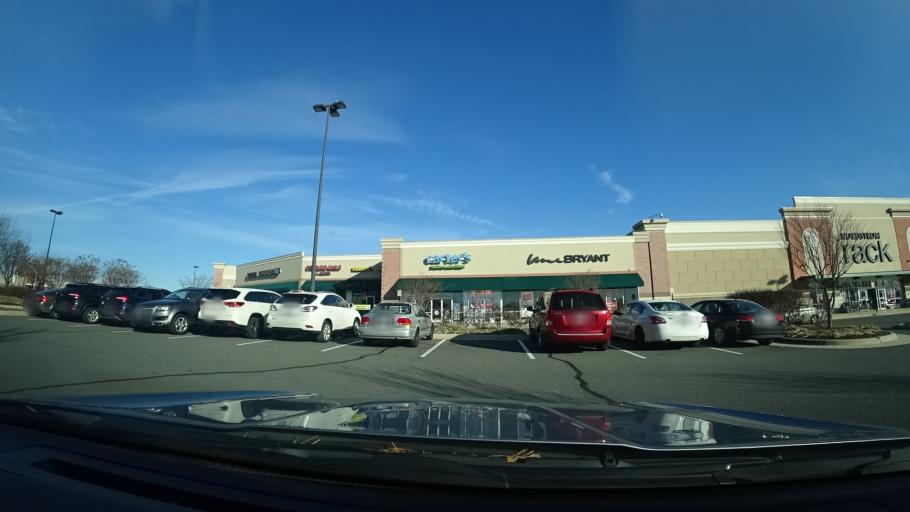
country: US
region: Virginia
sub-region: Loudoun County
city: Dulles Town Center
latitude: 39.0253
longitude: -77.4231
